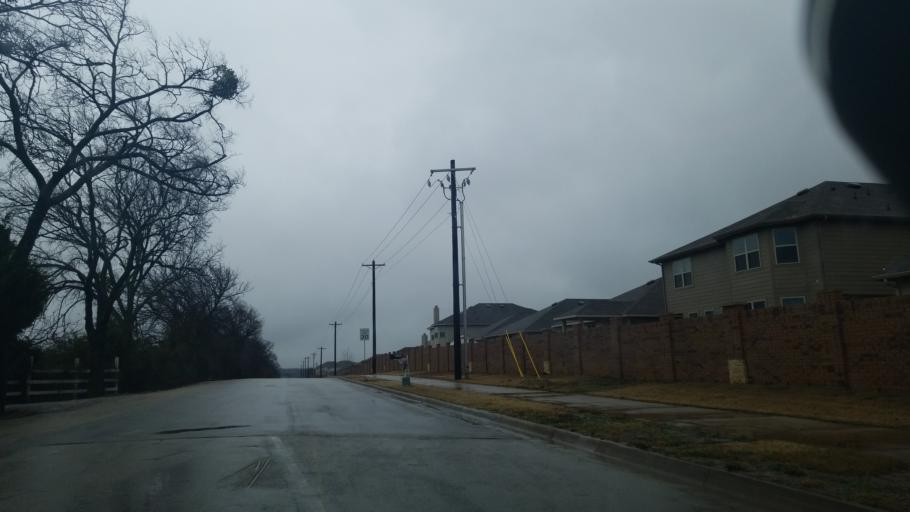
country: US
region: Texas
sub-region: Denton County
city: Corinth
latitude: 33.1782
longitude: -97.0747
